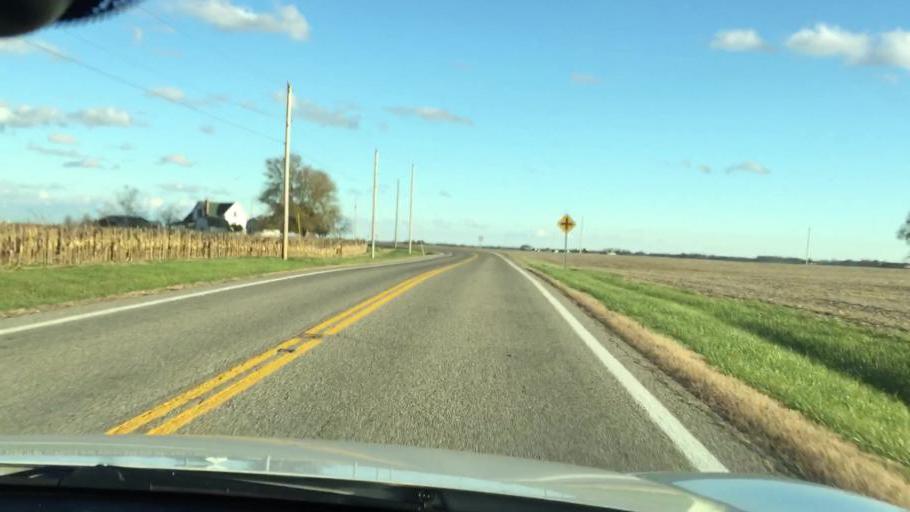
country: US
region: Ohio
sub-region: Champaign County
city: North Lewisburg
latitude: 40.1896
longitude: -83.5204
